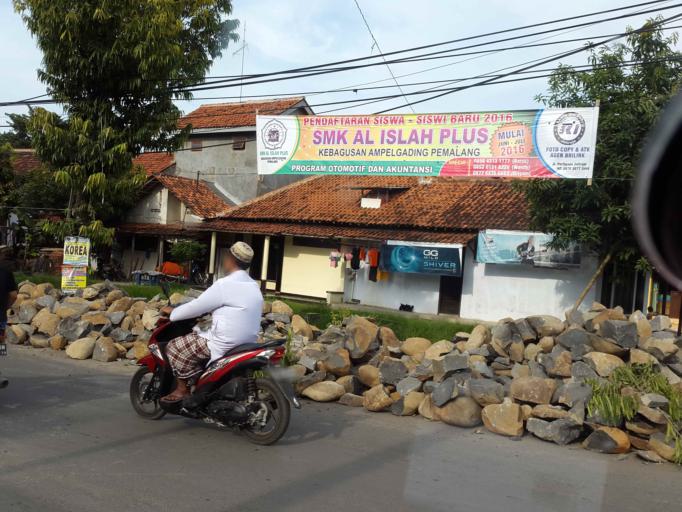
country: ID
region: Central Java
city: Comal
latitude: -6.8662
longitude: 109.5220
